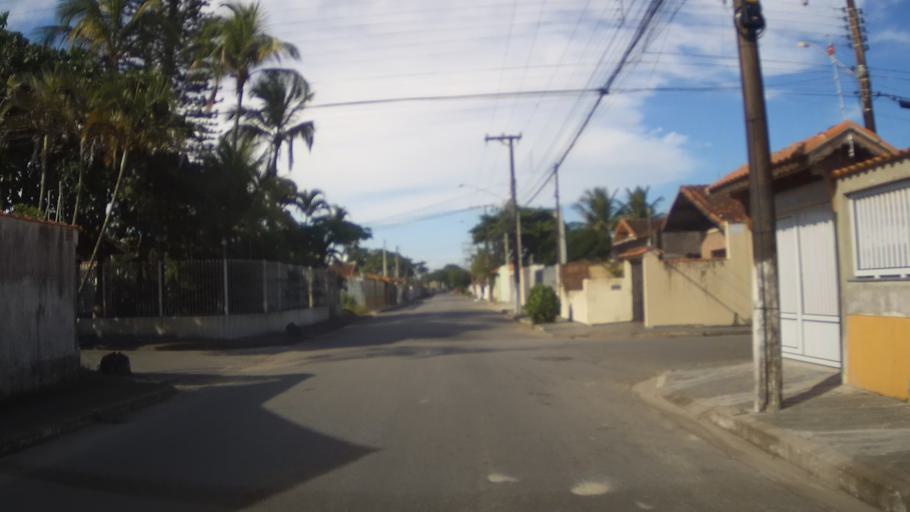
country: BR
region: Sao Paulo
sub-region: Itanhaem
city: Itanhaem
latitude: -24.1652
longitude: -46.7532
